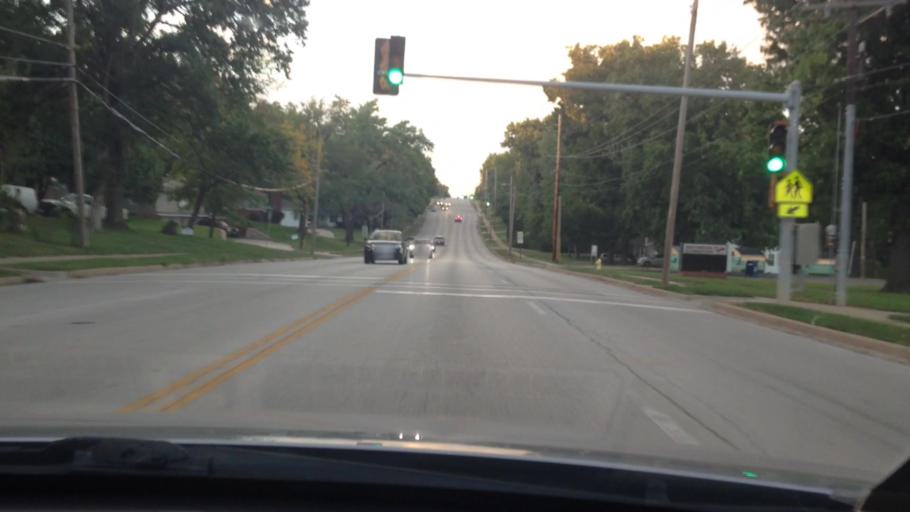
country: US
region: Missouri
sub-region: Jackson County
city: Raytown
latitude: 38.9766
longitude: -94.4648
